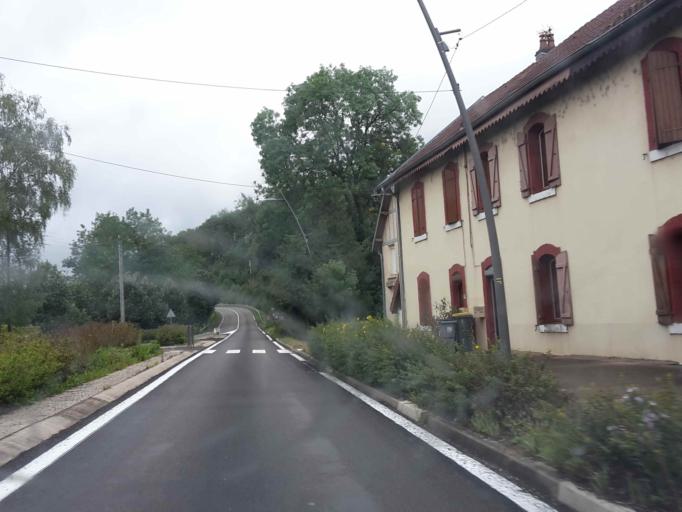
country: FR
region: Franche-Comte
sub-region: Departement du Doubs
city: Novillars
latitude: 47.2845
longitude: 6.1335
